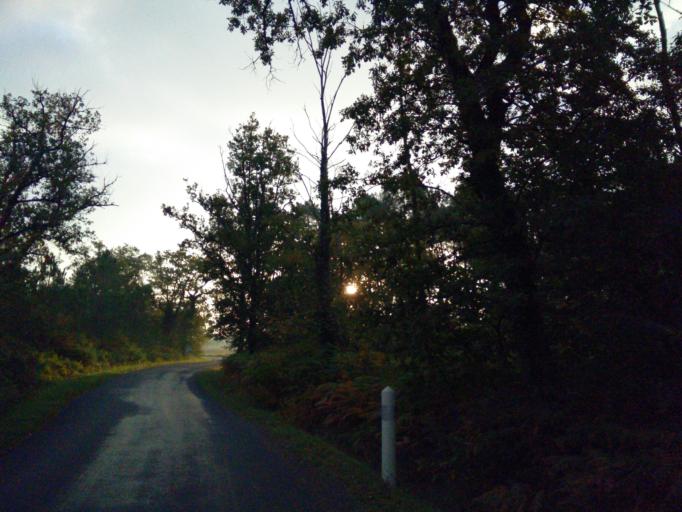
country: FR
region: Aquitaine
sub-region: Departement de la Dordogne
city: Rouffignac-Saint-Cernin-de-Reilhac
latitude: 45.0139
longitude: 0.9623
